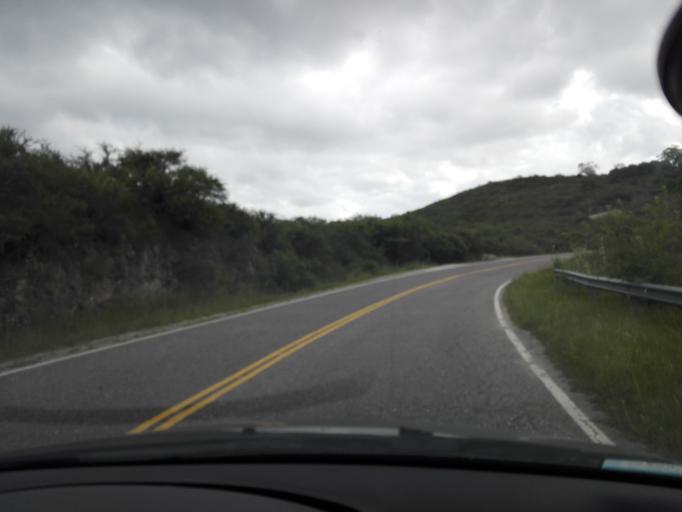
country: AR
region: Cordoba
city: Alta Gracia
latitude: -31.5916
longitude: -64.5174
